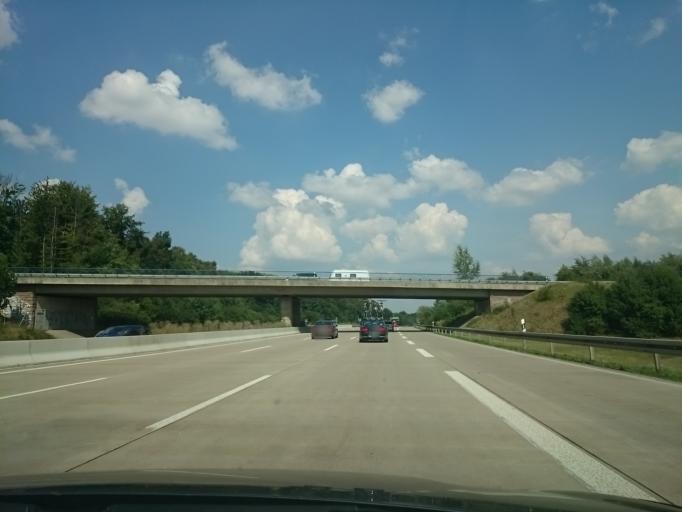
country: DE
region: Saxony
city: Hainichen
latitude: 50.9846
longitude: 13.0982
